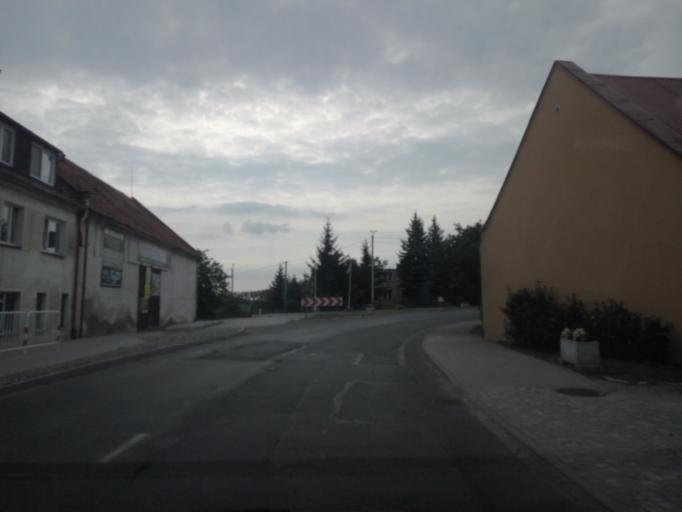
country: PL
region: Lower Silesian Voivodeship
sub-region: Powiat strzelinski
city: Strzelin
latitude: 50.8271
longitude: 17.0612
